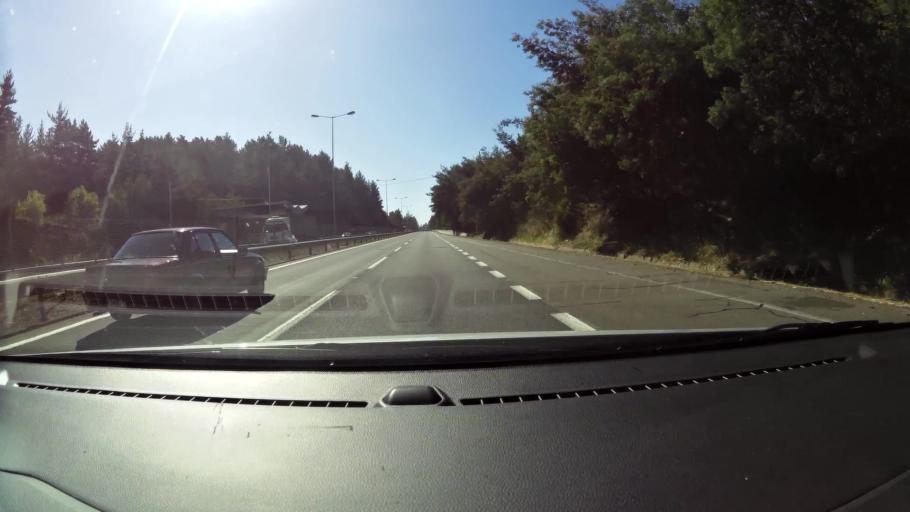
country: CL
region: Valparaiso
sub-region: Provincia de Valparaiso
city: Vina del Mar
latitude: -33.1614
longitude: -71.5415
